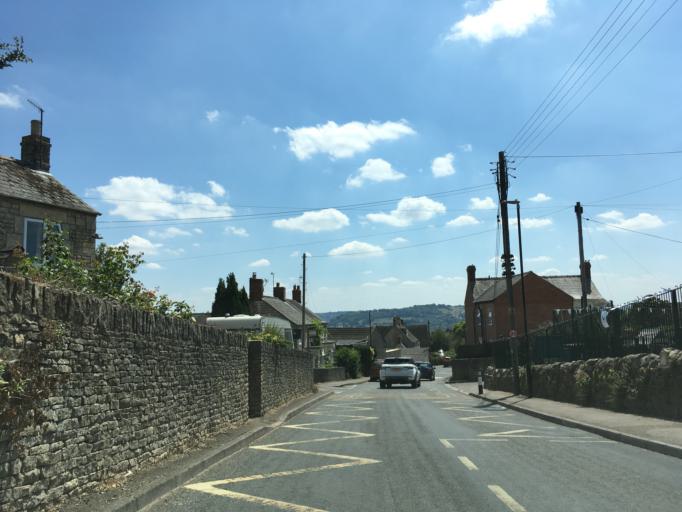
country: GB
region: England
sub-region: Gloucestershire
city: Stroud
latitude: 51.7626
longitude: -2.2334
